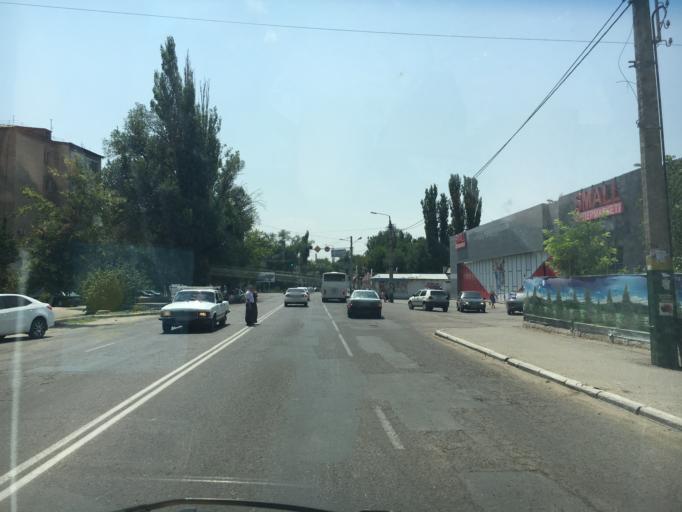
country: KZ
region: Zhambyl
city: Taraz
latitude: 42.8723
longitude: 71.3787
